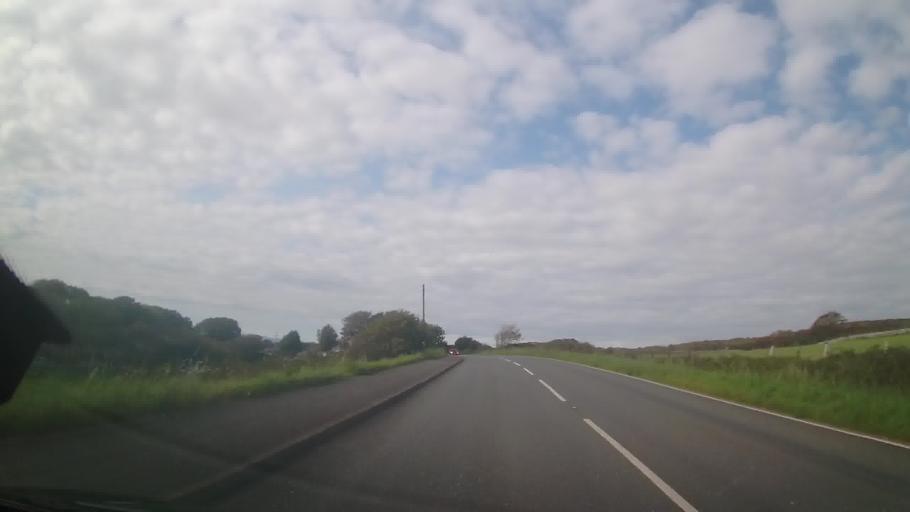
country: GB
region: Wales
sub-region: Gwynedd
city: Dyffryn Ardudwy
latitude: 52.7710
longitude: -4.0909
